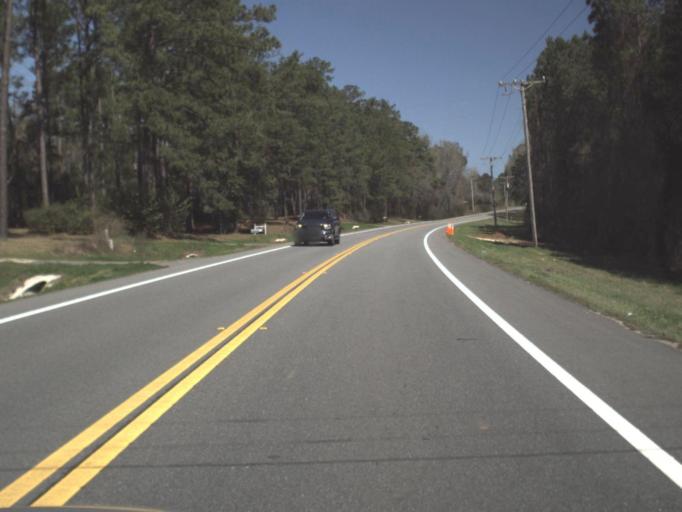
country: US
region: Florida
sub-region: Gadsden County
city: Quincy
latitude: 30.5198
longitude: -84.6080
